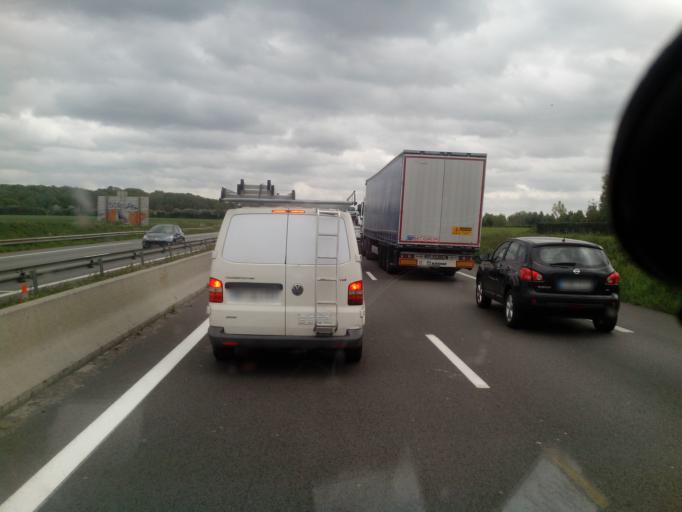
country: FR
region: Nord-Pas-de-Calais
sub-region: Departement du Nord
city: Ennetieres-en-Weppes
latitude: 50.6346
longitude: 2.9479
